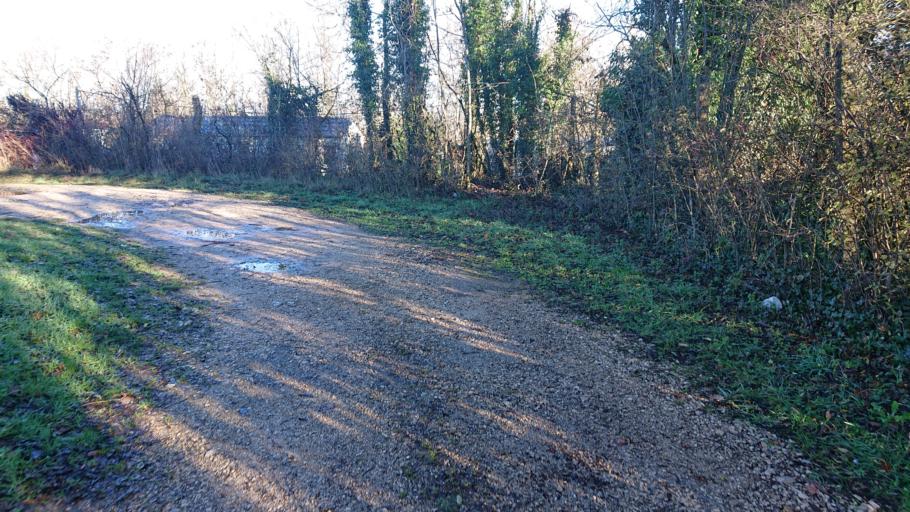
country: FR
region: Franche-Comte
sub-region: Departement du Jura
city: Clairvaux-les-Lacs
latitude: 46.5768
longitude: 5.7408
